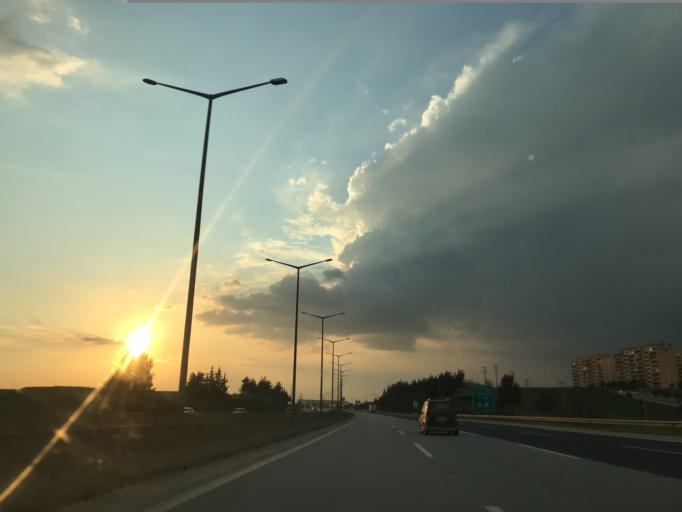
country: TR
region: Adana
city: Seyhan
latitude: 37.0296
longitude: 35.2164
